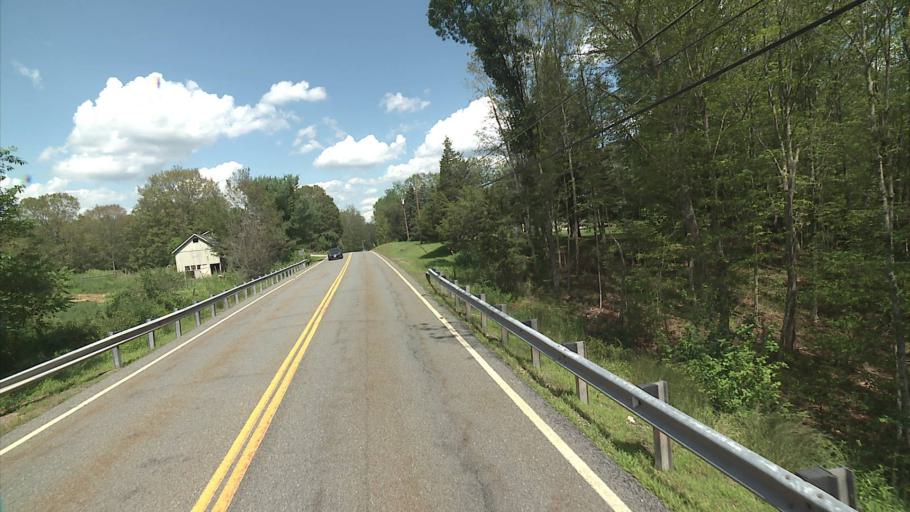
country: US
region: Connecticut
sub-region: Tolland County
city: Mansfield City
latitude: 41.7902
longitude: -72.1768
